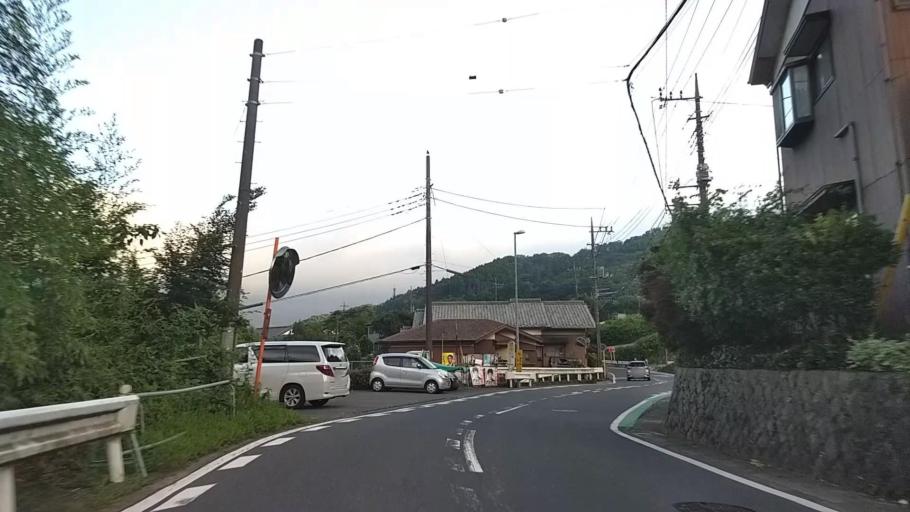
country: JP
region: Kanagawa
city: Atsugi
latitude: 35.4867
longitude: 139.2723
